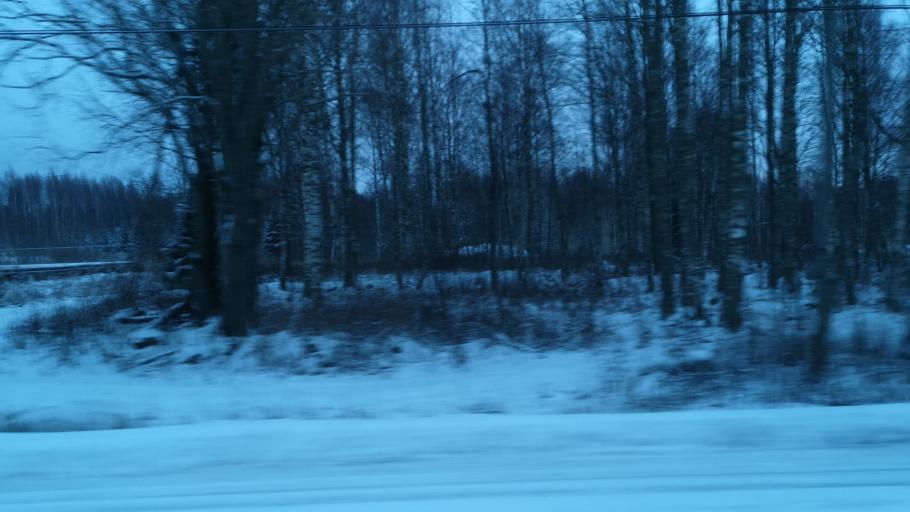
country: FI
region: Southern Savonia
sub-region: Savonlinna
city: Enonkoski
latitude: 62.0679
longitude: 28.7371
